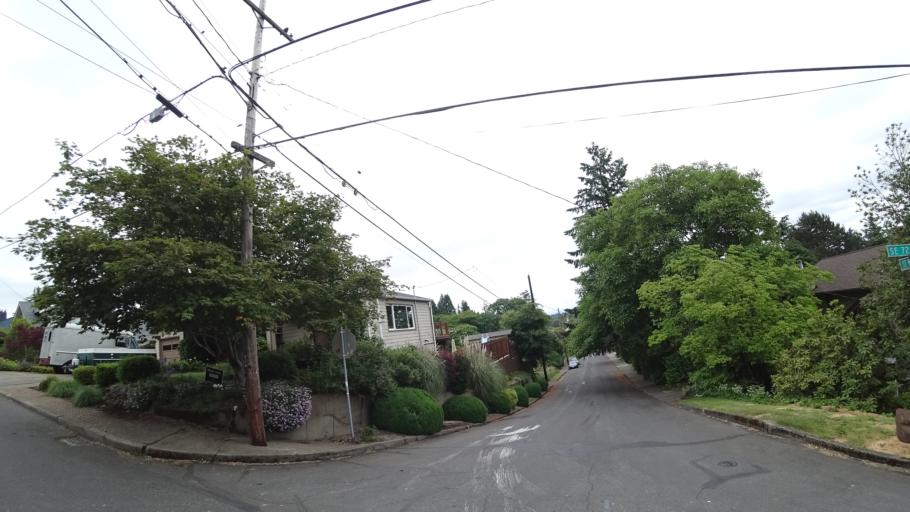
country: US
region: Oregon
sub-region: Multnomah County
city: Lents
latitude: 45.5103
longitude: -122.5890
